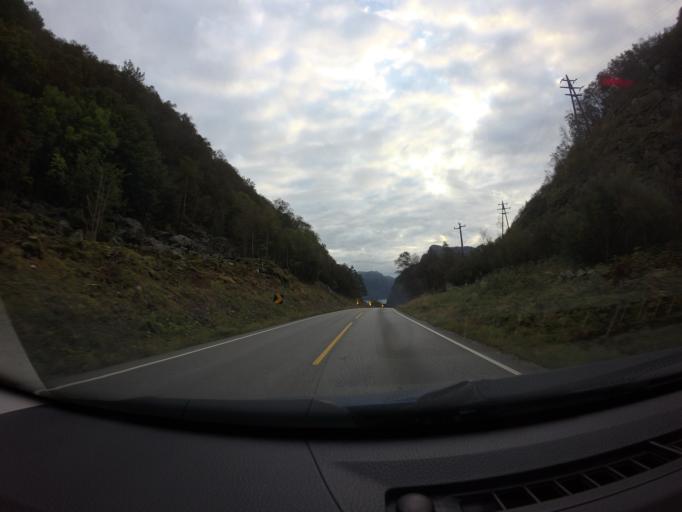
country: NO
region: Rogaland
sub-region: Forsand
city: Forsand
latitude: 58.8398
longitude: 6.1486
